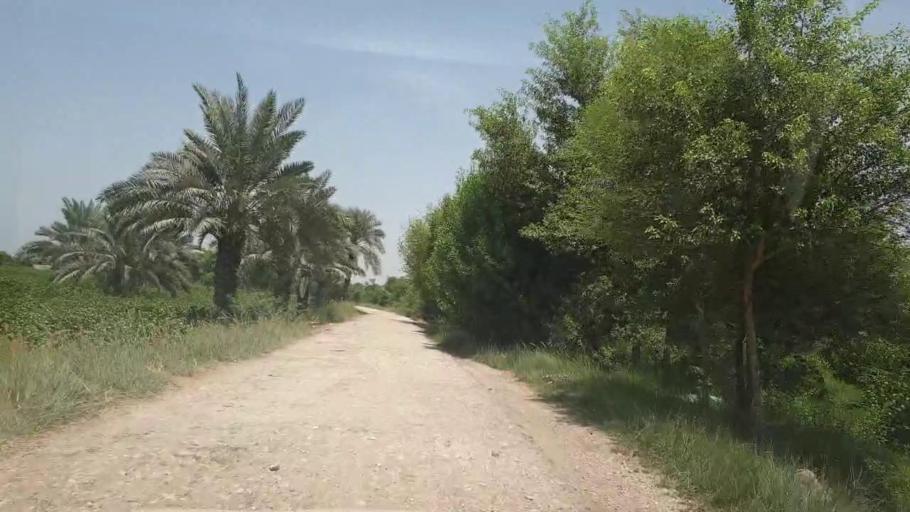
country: PK
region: Sindh
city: Bozdar
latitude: 27.1738
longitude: 68.6283
